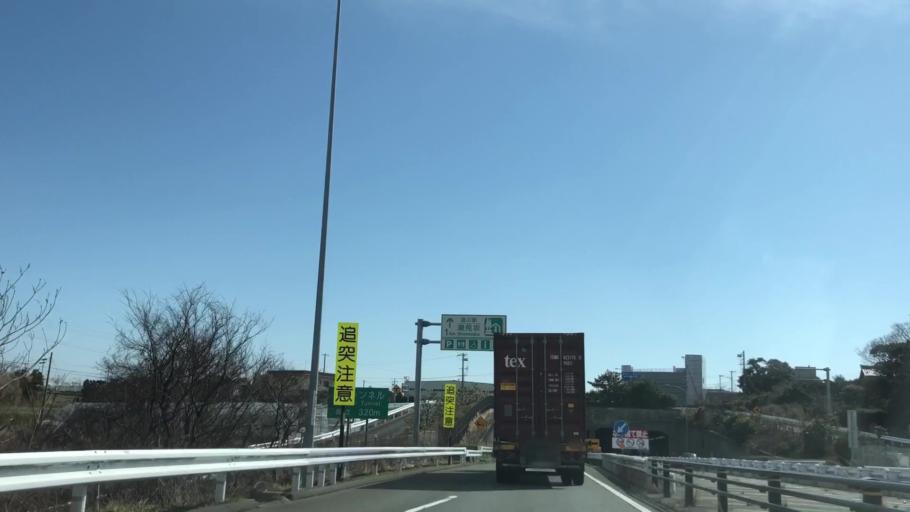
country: JP
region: Shizuoka
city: Kosai-shi
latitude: 34.6873
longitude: 137.4902
